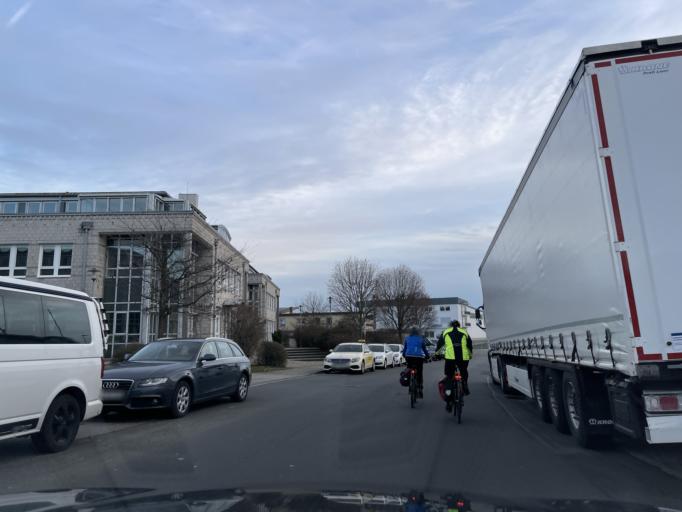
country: DE
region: Hesse
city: Kelsterbach
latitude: 50.0495
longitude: 8.5434
